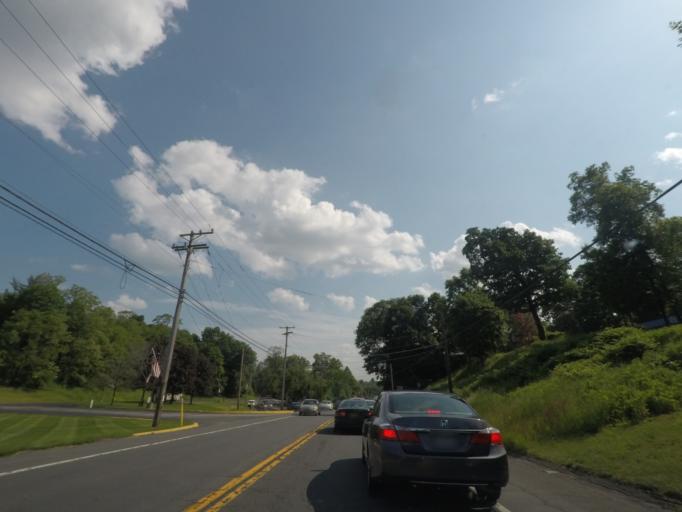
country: US
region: New York
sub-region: Orange County
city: Balmville
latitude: 41.5375
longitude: -74.0134
